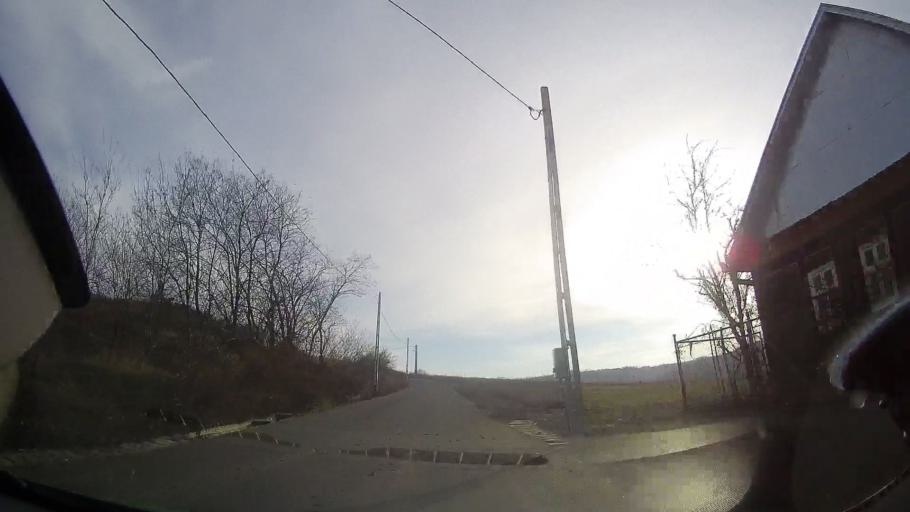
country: RO
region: Bihor
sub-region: Comuna Sarbi
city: Burzuc
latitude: 47.1376
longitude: 22.1836
